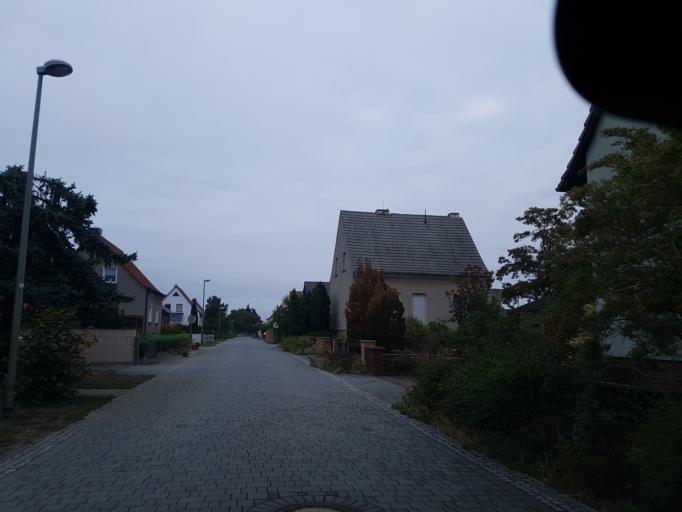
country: DE
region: Saxony-Anhalt
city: Elster
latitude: 51.8268
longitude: 12.8368
